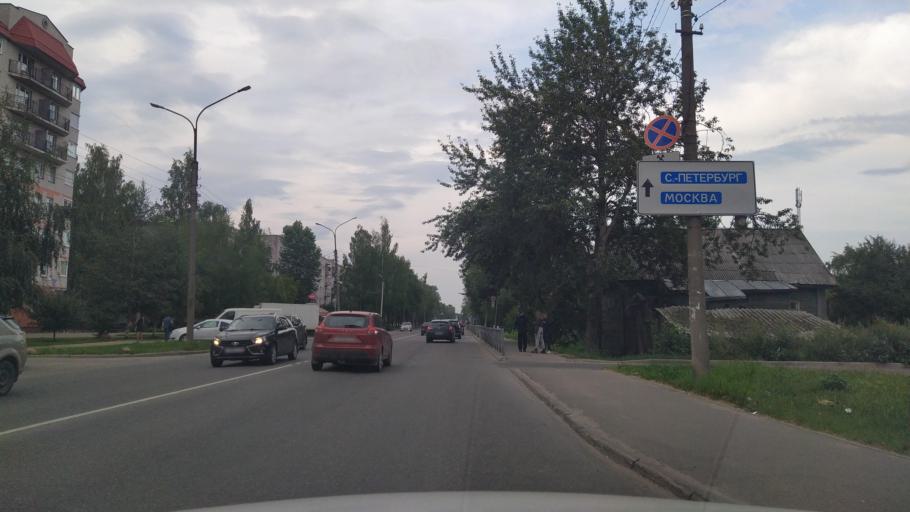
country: RU
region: Novgorod
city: Velikiy Novgorod
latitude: 58.5167
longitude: 31.2471
